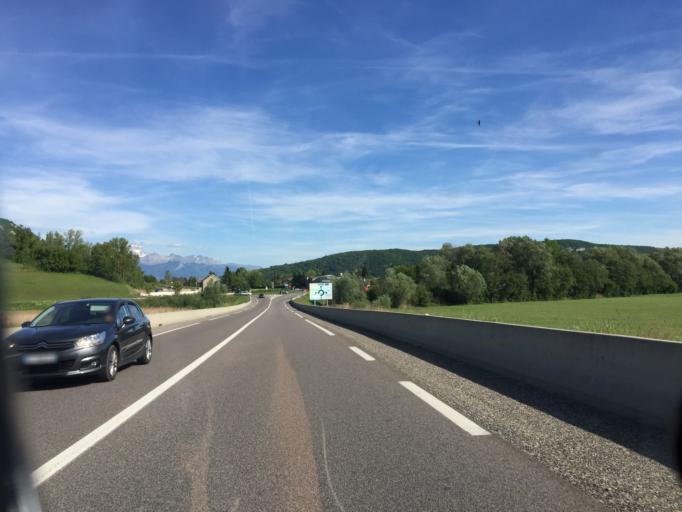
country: FR
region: Rhone-Alpes
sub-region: Departement de la Haute-Savoie
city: La Balme-de-Sillingy
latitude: 45.9565
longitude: 6.0359
